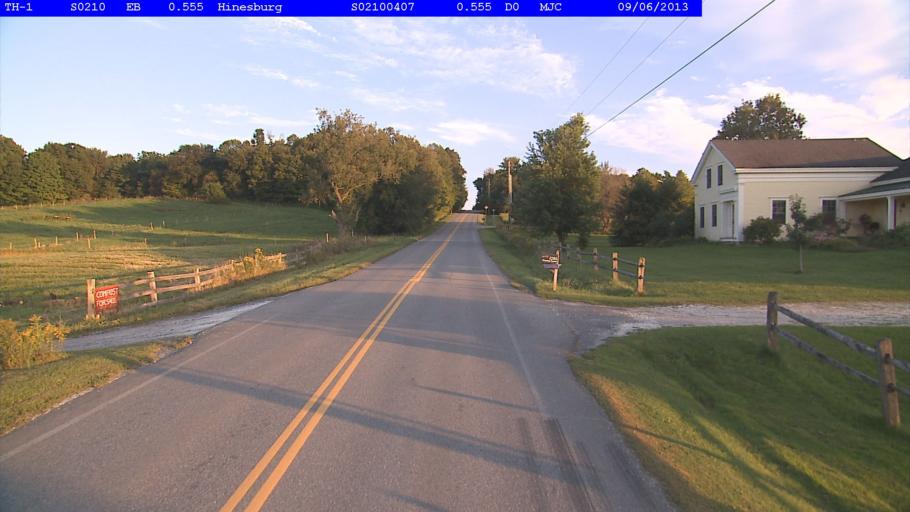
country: US
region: Vermont
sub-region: Chittenden County
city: Hinesburg
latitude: 44.3560
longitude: -73.1556
